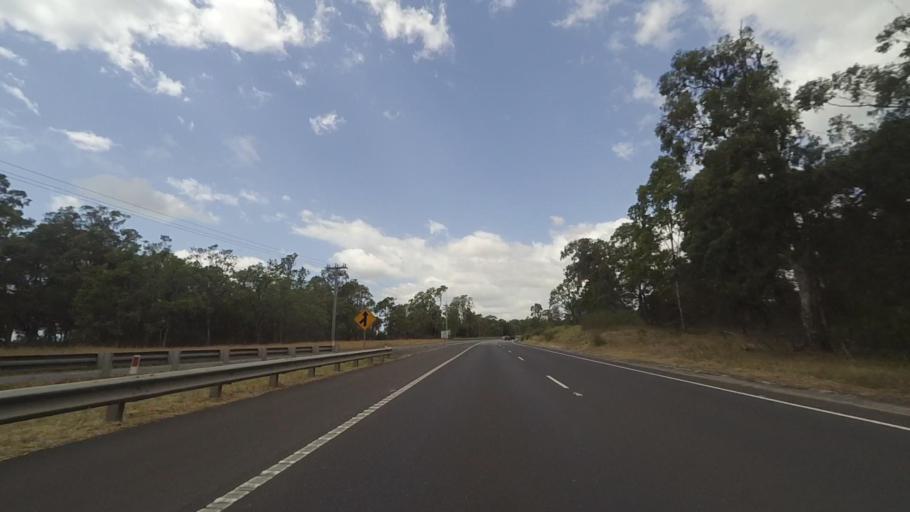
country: AU
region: New South Wales
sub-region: Wollongong
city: Dapto
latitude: -34.5304
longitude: 150.7871
